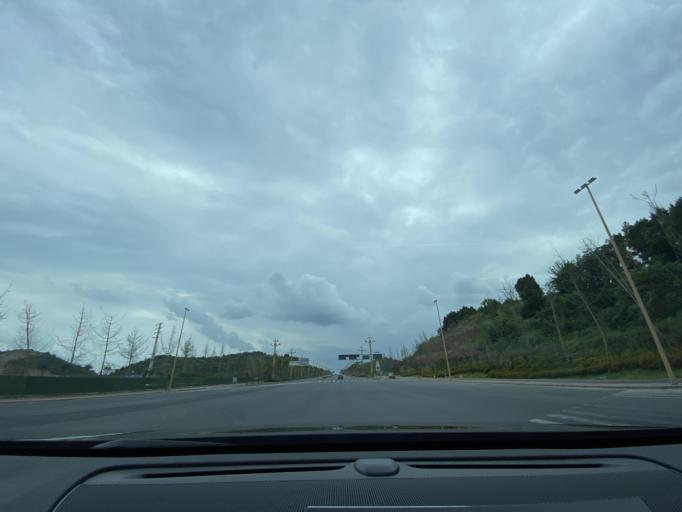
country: CN
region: Sichuan
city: Jiancheng
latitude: 30.4562
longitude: 104.4958
